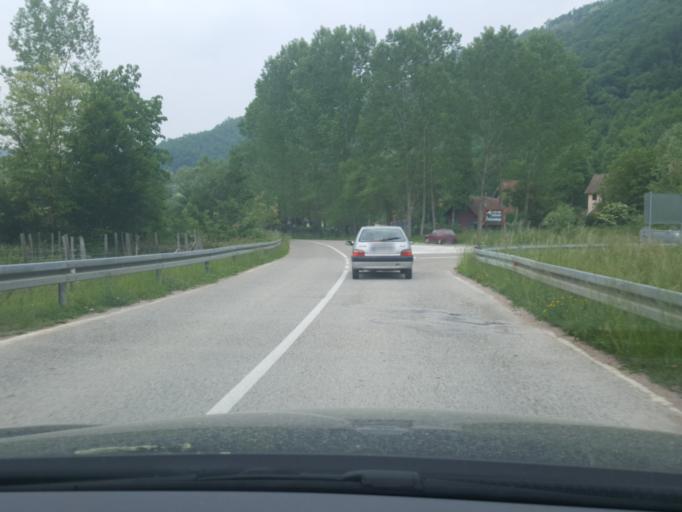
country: RS
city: Kamenica
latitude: 44.2465
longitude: 19.7632
